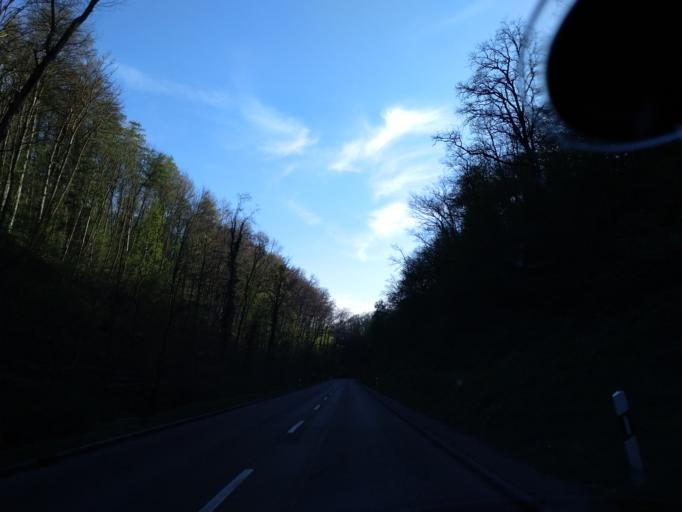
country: DE
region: Baden-Wuerttemberg
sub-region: Regierungsbezirk Stuttgart
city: Kirchberg an der Jagst
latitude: 49.2101
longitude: 9.9951
